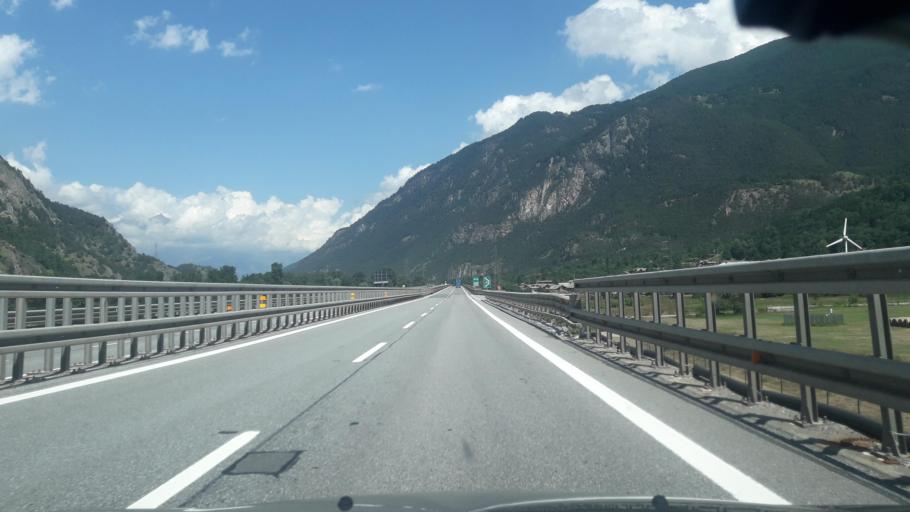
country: IT
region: Piedmont
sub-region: Provincia di Torino
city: Oulx
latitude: 45.0426
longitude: 6.8384
